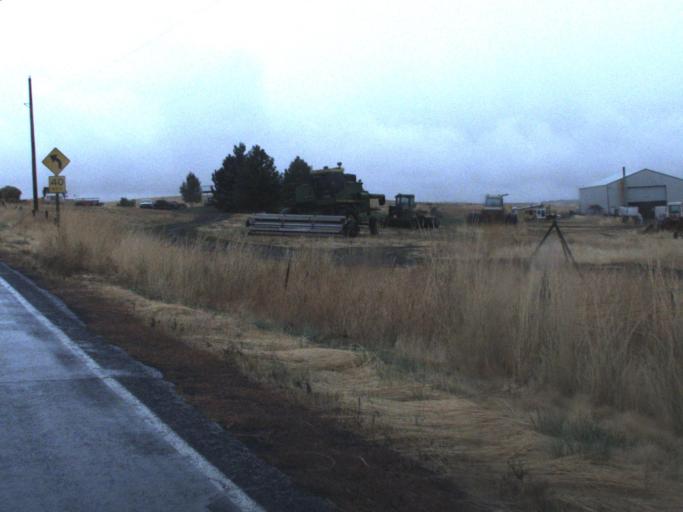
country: US
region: Washington
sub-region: Lincoln County
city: Davenport
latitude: 47.3410
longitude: -118.0045
